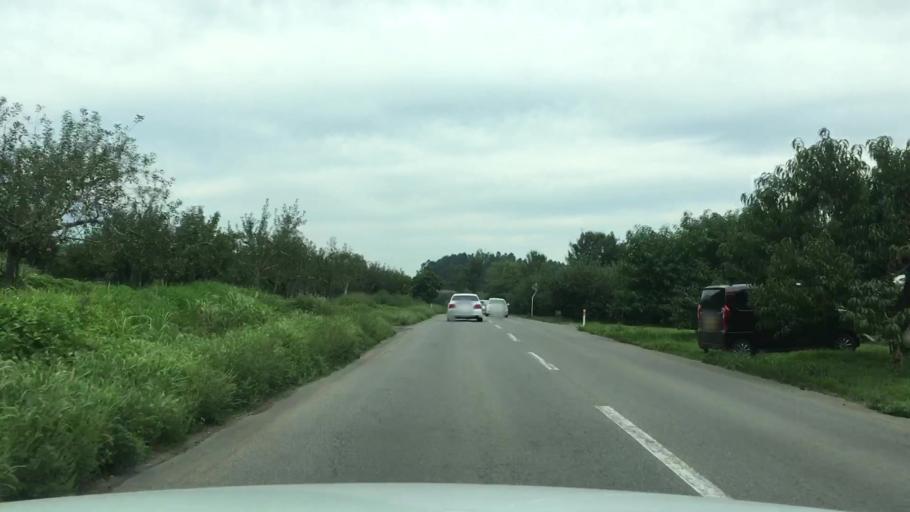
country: JP
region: Aomori
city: Hirosaki
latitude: 40.6423
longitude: 140.4333
